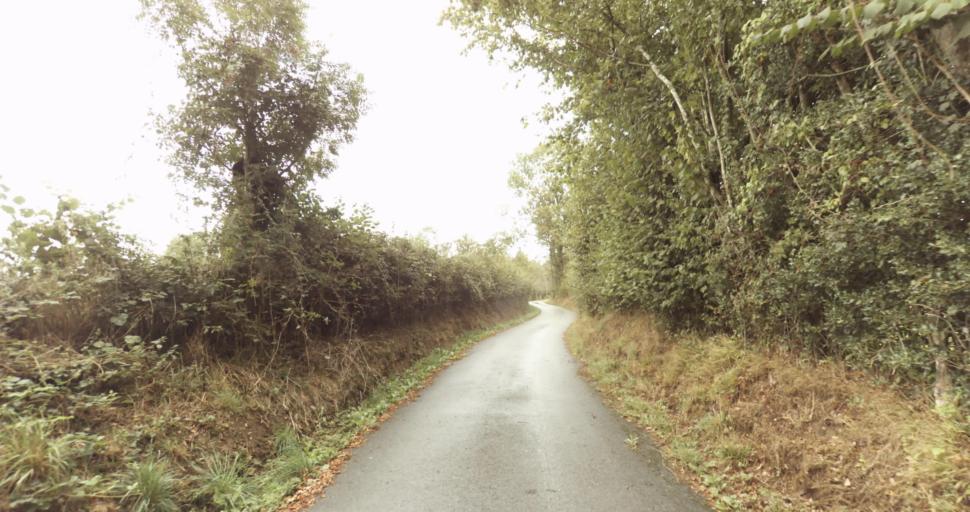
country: FR
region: Lower Normandy
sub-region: Departement de l'Orne
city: Sainte-Gauburge-Sainte-Colombe
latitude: 48.7126
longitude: 0.3838
